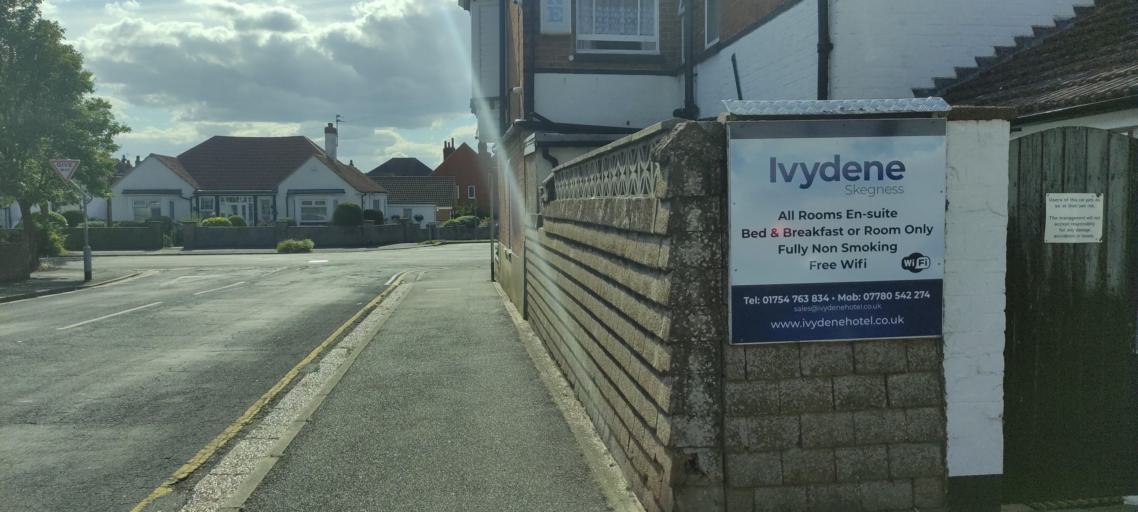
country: GB
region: England
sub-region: Lincolnshire
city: Skegness
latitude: 53.1391
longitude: 0.3430
